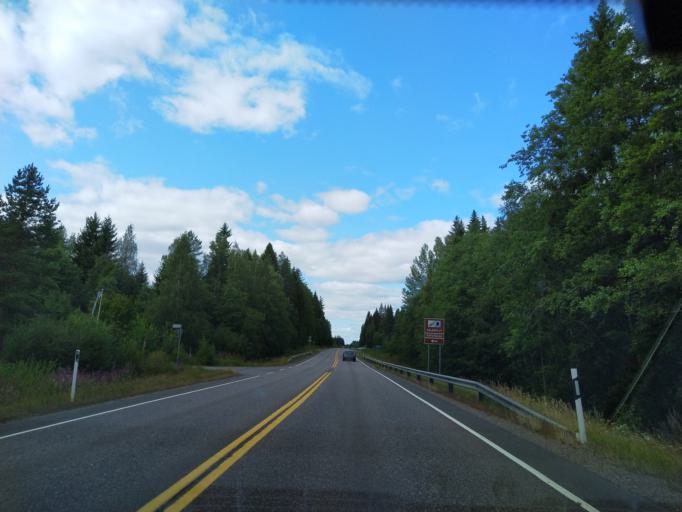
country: FI
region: Haeme
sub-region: Haemeenlinna
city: Renko
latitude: 60.7610
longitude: 24.2862
